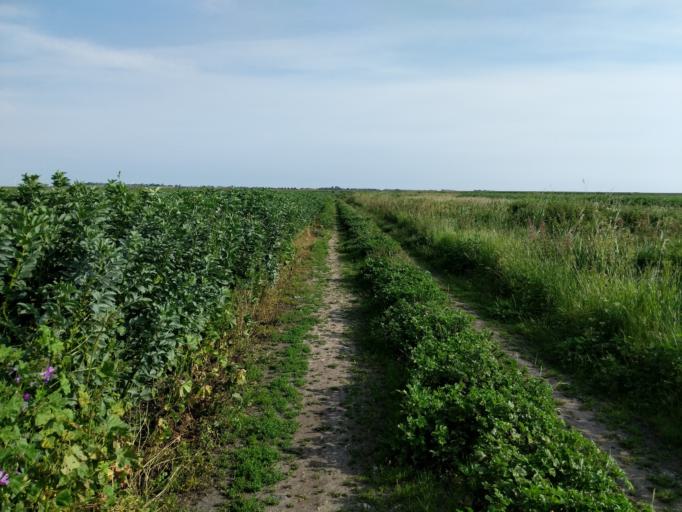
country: GB
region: England
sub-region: Kent
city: Faversham
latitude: 51.3389
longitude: 0.9107
